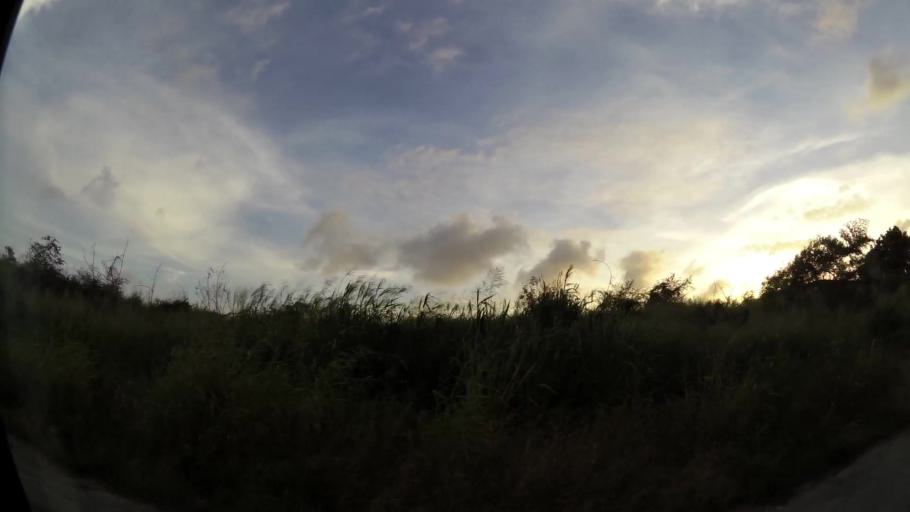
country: BB
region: Saint Philip
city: Crane
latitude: 13.0972
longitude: -59.4940
